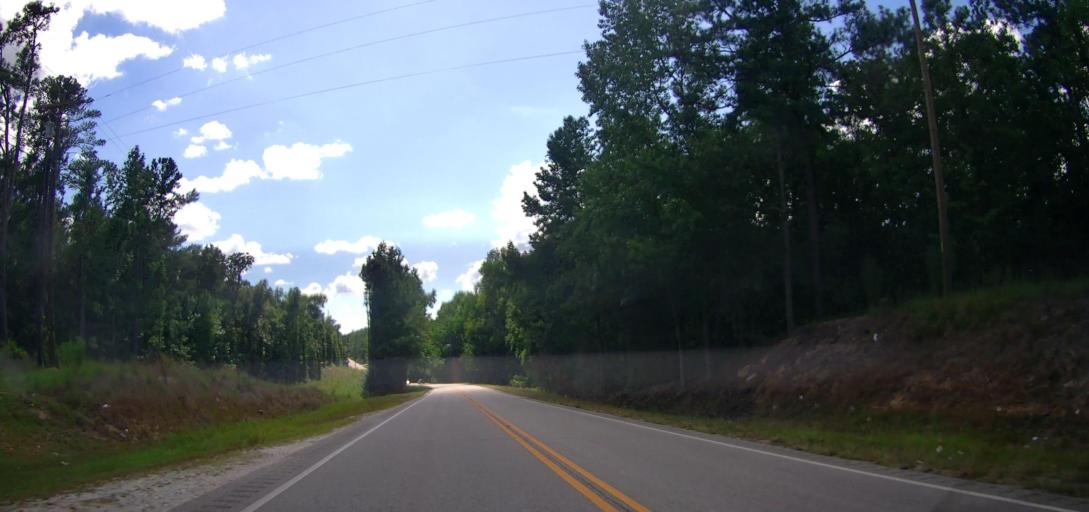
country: US
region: Alabama
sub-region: Macon County
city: Tuskegee
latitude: 32.4621
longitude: -85.6071
